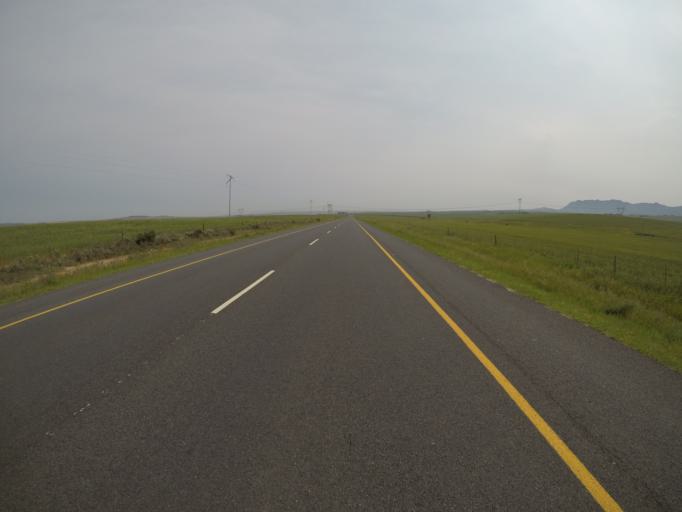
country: ZA
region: Western Cape
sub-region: West Coast District Municipality
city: Malmesbury
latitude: -33.4978
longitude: 18.8313
